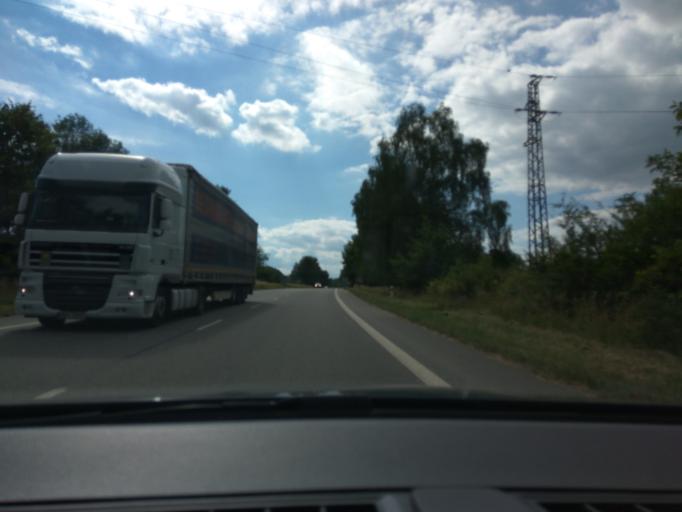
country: CZ
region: Jihocesky
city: Kovarov
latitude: 49.5030
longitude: 14.1726
